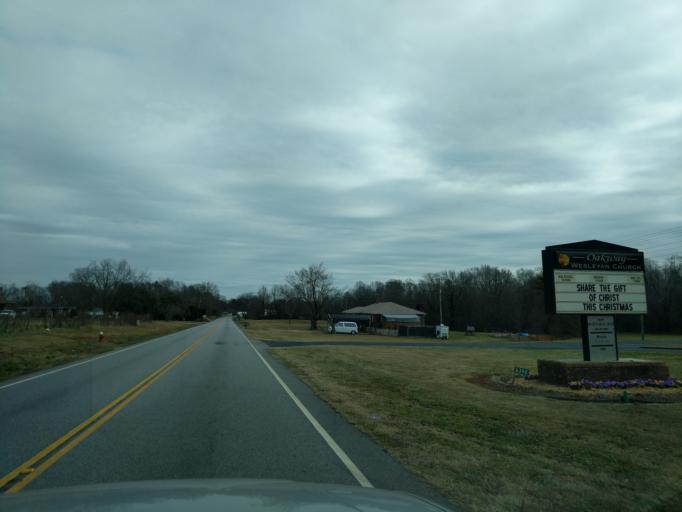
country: US
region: South Carolina
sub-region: Oconee County
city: Seneca
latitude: 34.5996
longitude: -83.0129
